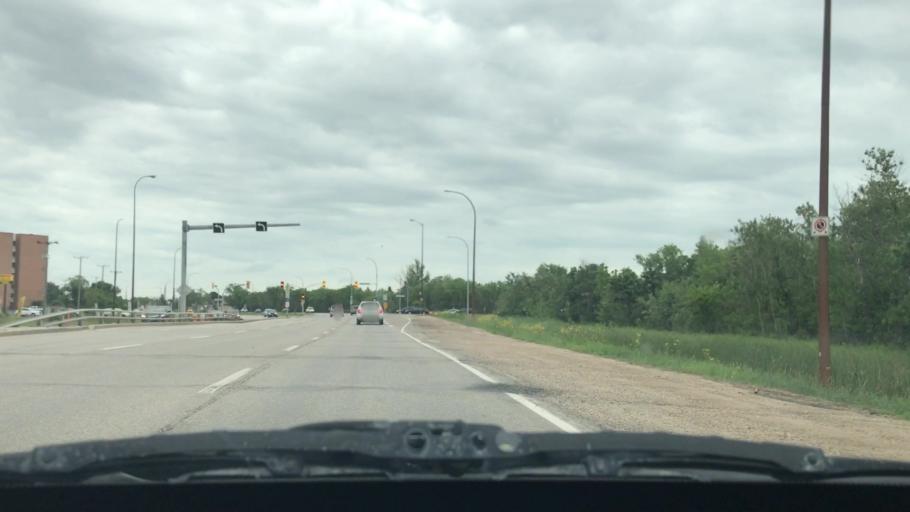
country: CA
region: Manitoba
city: Winnipeg
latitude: 49.8572
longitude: -97.0902
